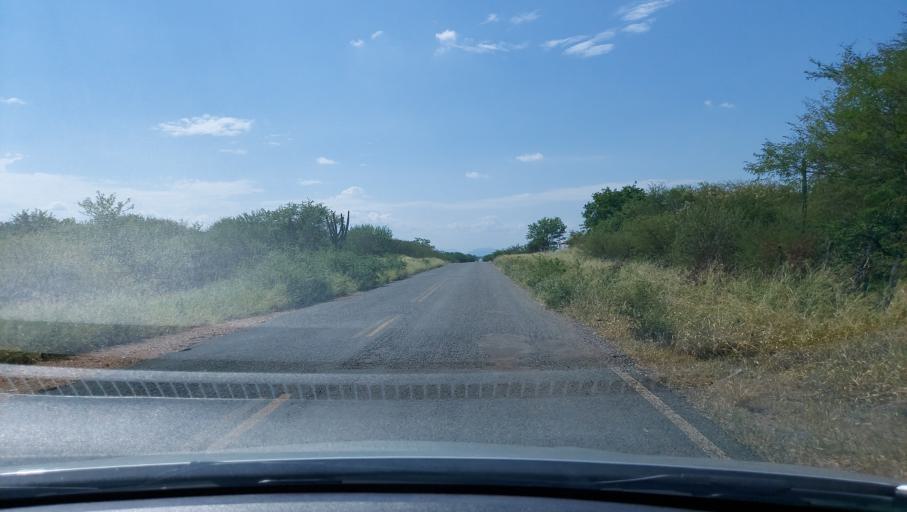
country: BR
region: Bahia
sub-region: Oliveira Dos Brejinhos
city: Beira Rio
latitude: -12.1642
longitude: -42.5484
